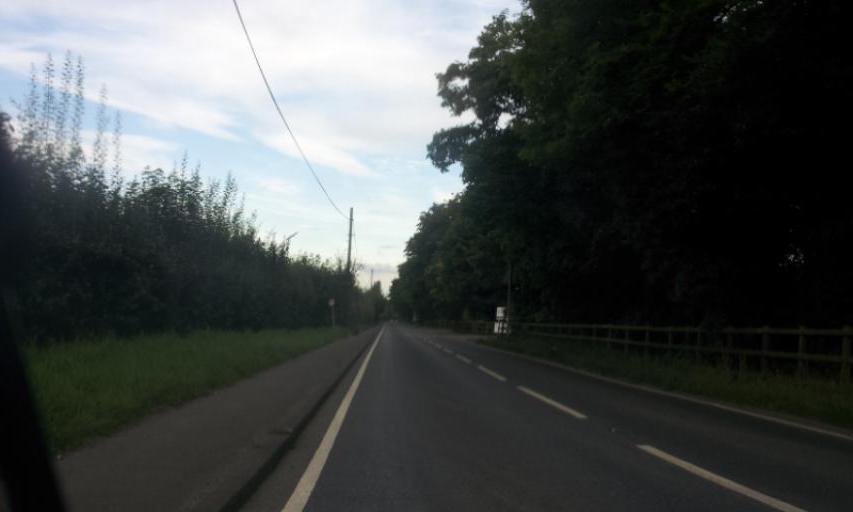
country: GB
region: England
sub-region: Kent
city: Maidstone
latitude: 51.2297
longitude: 0.5204
